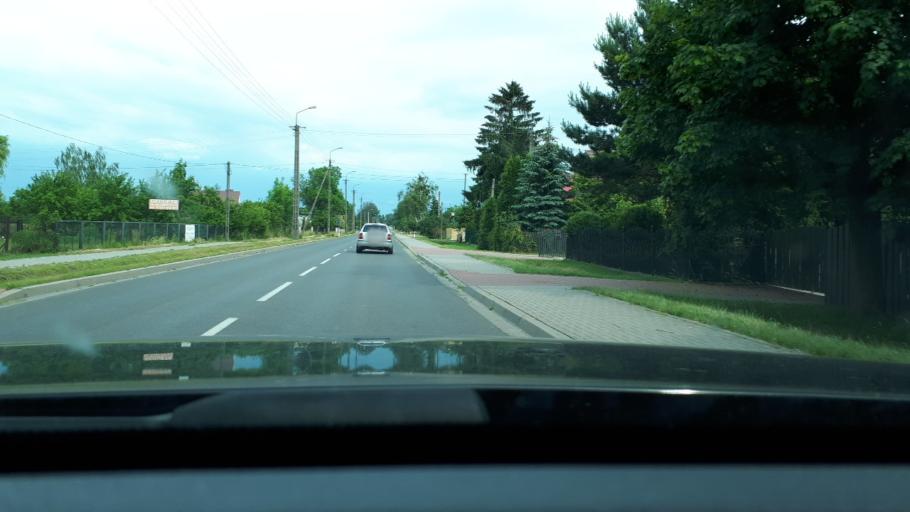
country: PL
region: Masovian Voivodeship
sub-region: Powiat warszawski zachodni
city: Kampinos
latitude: 52.2663
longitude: 20.4730
